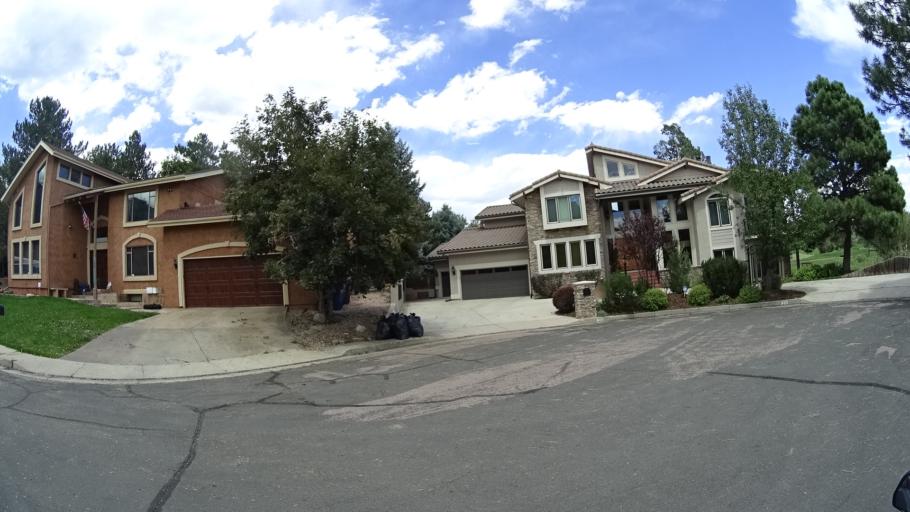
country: US
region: Colorado
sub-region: El Paso County
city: Stratmoor
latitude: 38.7809
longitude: -104.8289
